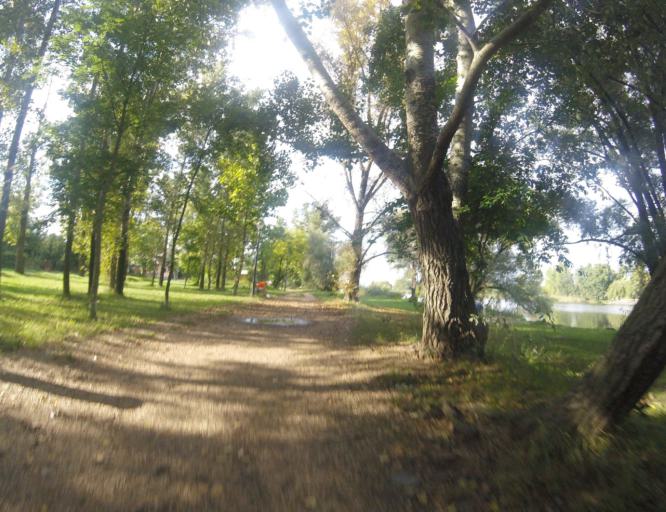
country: HU
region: Budapest
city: Budapest XXIII. keruelet
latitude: 47.3970
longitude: 19.1075
